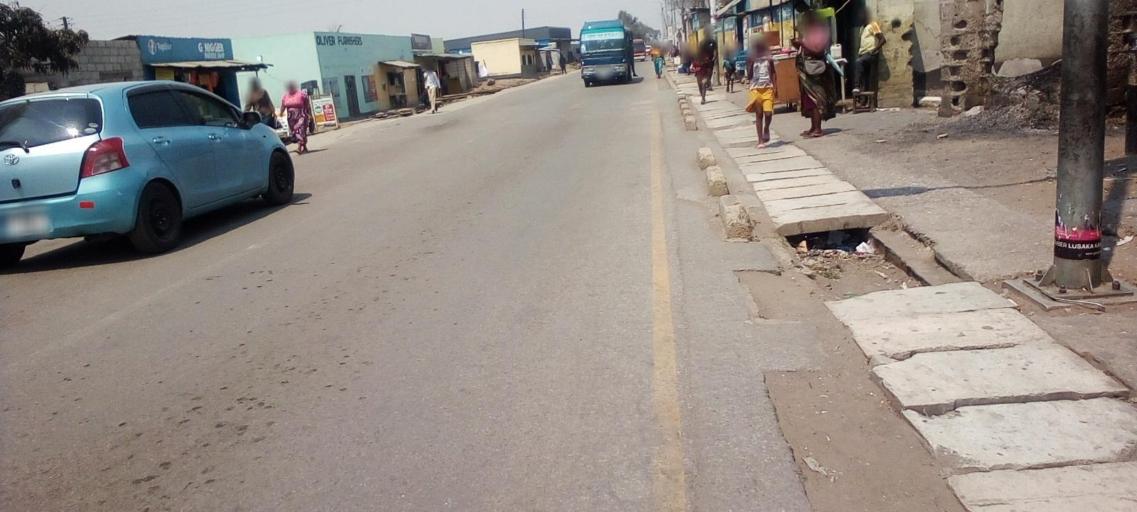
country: ZM
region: Lusaka
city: Lusaka
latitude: -15.4362
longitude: 28.2584
